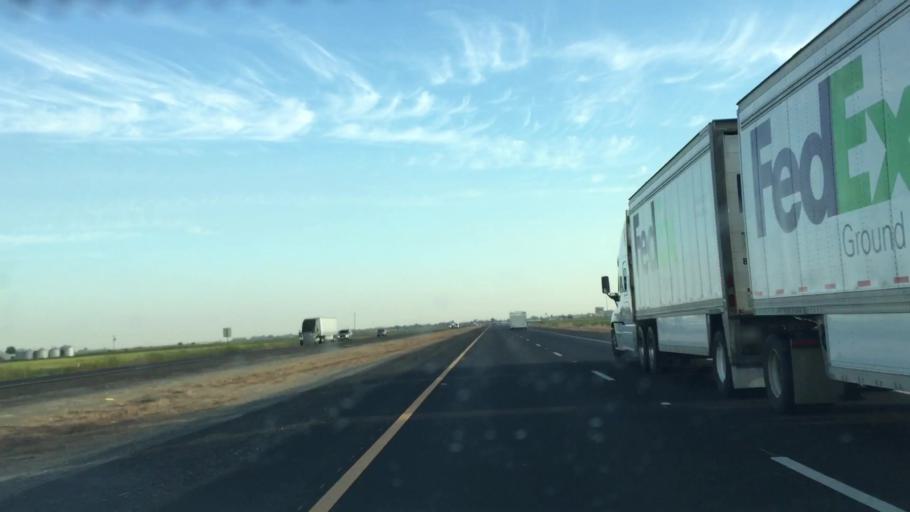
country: US
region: California
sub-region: Glenn County
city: Willows
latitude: 39.4681
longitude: -122.1951
